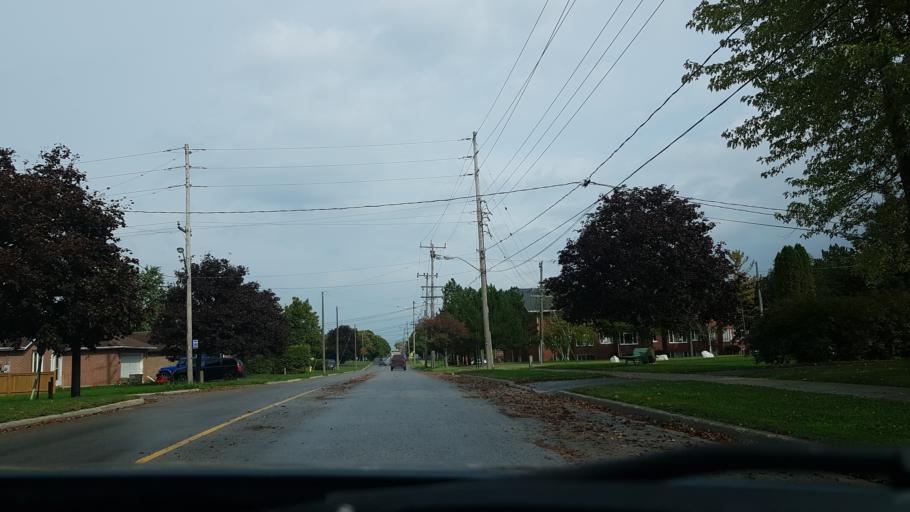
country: CA
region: Ontario
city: Omemee
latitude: 44.3560
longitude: -78.7596
